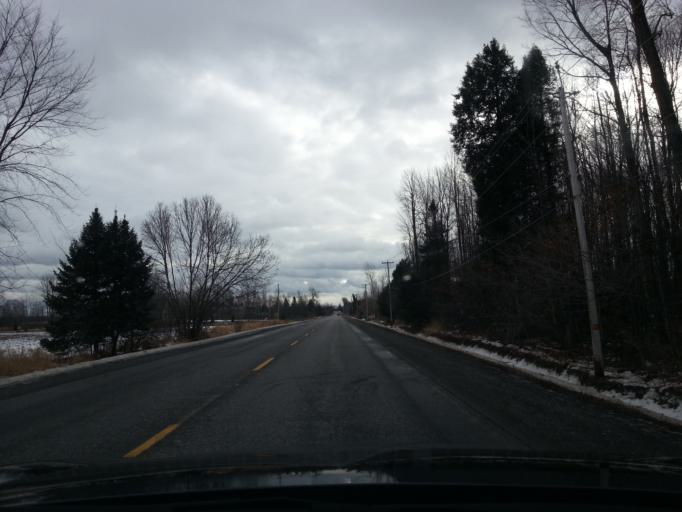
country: CA
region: Ontario
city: Bells Corners
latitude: 45.2335
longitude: -75.7245
